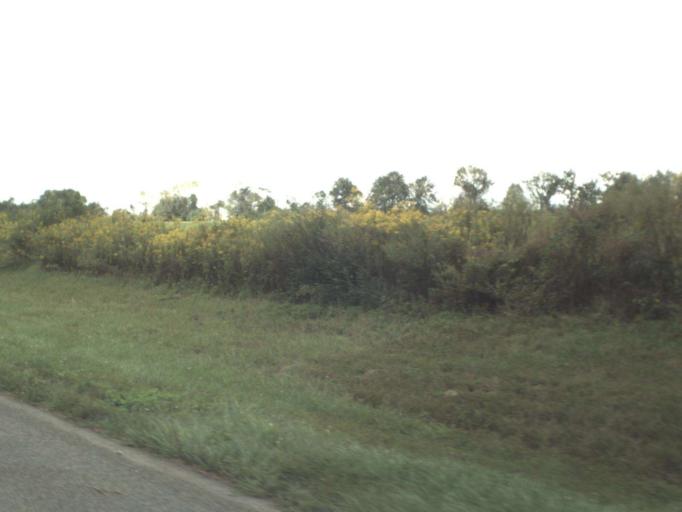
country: US
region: Florida
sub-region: Washington County
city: Chipley
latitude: 30.8583
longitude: -85.4969
